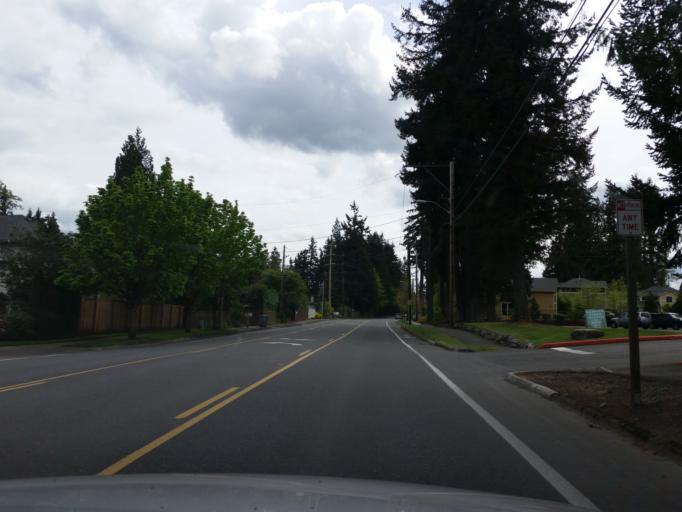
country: US
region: Washington
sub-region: King County
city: Redmond
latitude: 47.6840
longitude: -122.1642
